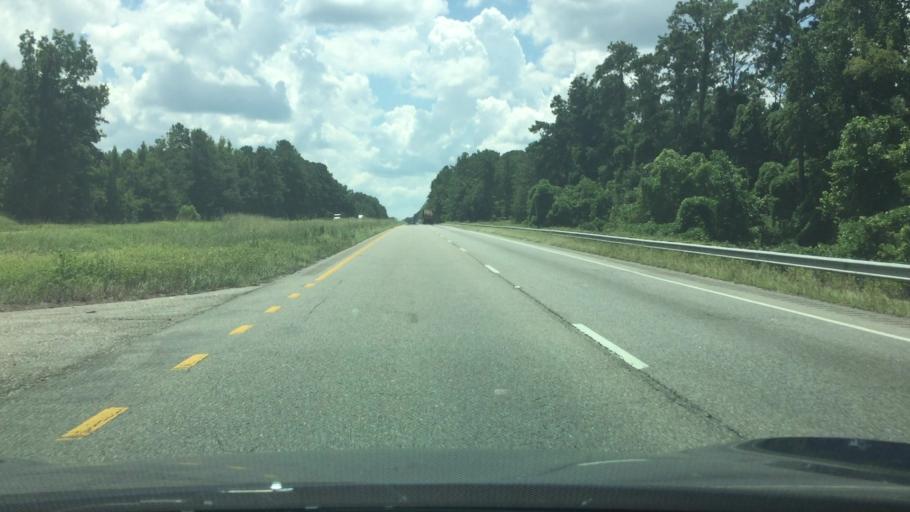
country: US
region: Alabama
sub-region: Montgomery County
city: Pike Road
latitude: 32.0892
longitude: -86.0645
